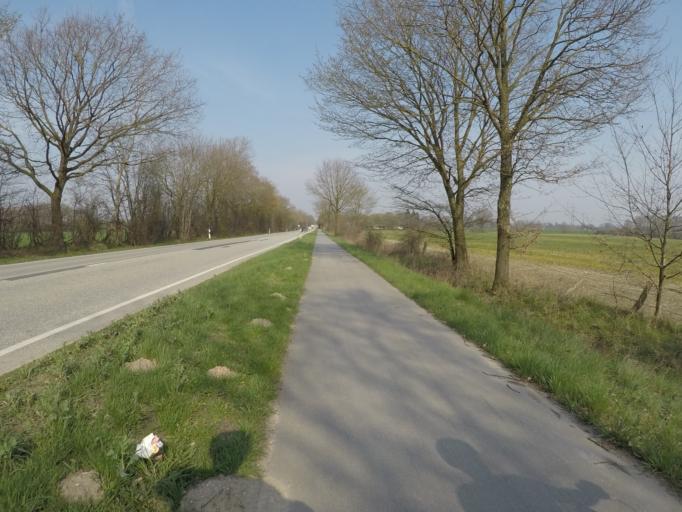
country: DE
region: Schleswig-Holstein
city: Gross Niendorf
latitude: 53.8344
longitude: 10.2170
